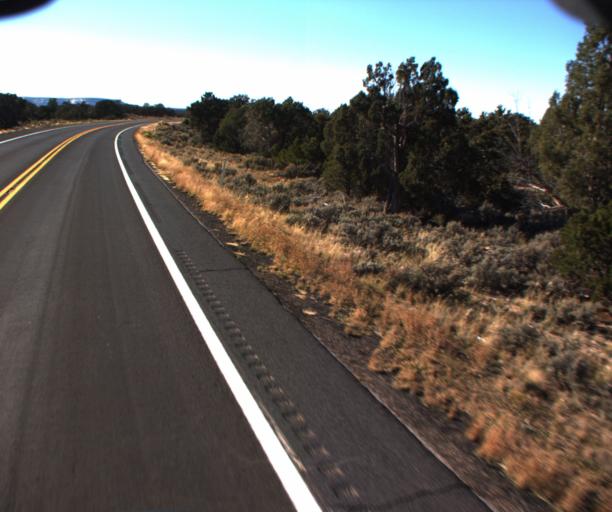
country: US
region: Arizona
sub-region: Coconino County
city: Kaibito
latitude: 36.5799
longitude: -110.8546
